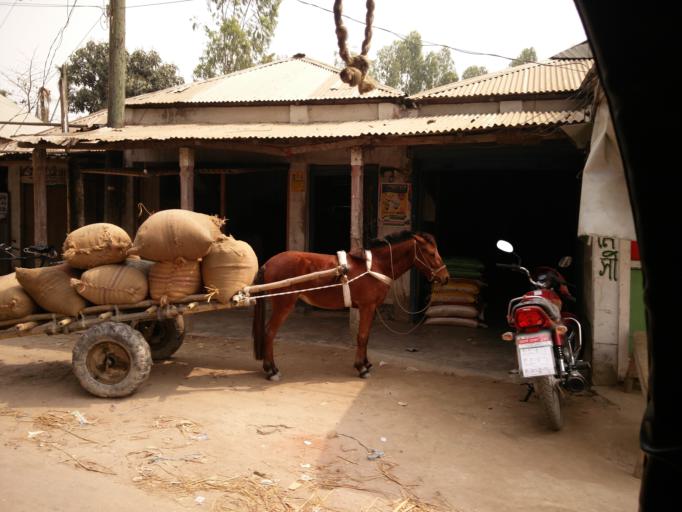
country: BD
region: Rangpur Division
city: Nageswari
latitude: 25.8899
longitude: 89.7089
